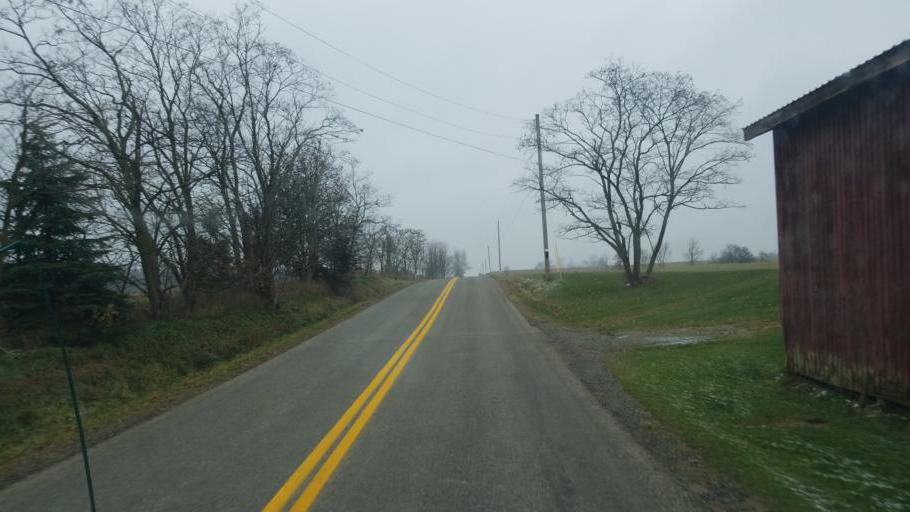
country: US
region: Ohio
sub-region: Huron County
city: New London
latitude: 40.9941
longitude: -82.3546
